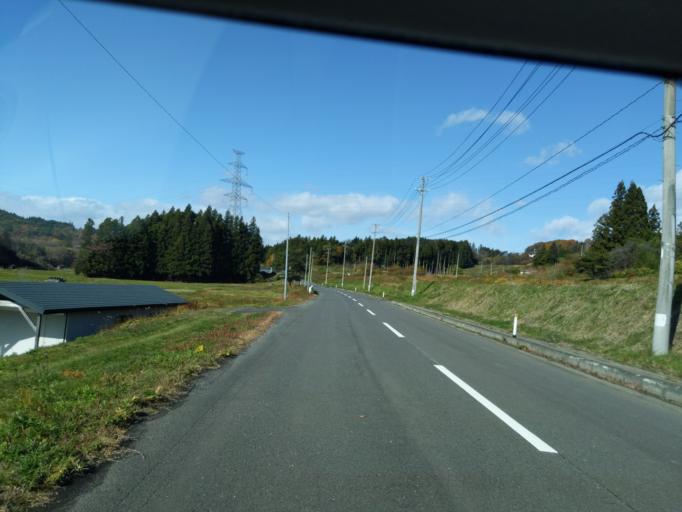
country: JP
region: Iwate
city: Ichinoseki
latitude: 39.0244
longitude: 141.1112
